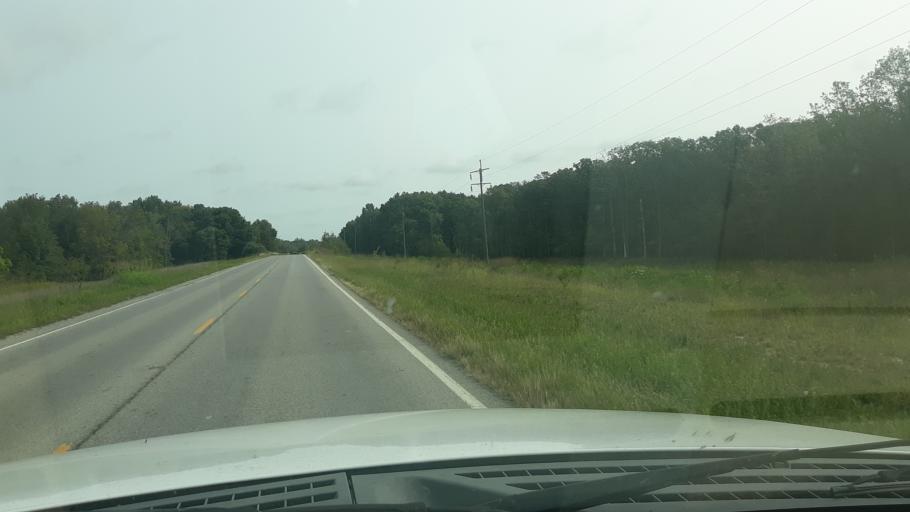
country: US
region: Illinois
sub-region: Saline County
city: Eldorado
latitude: 37.8824
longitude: -88.3895
